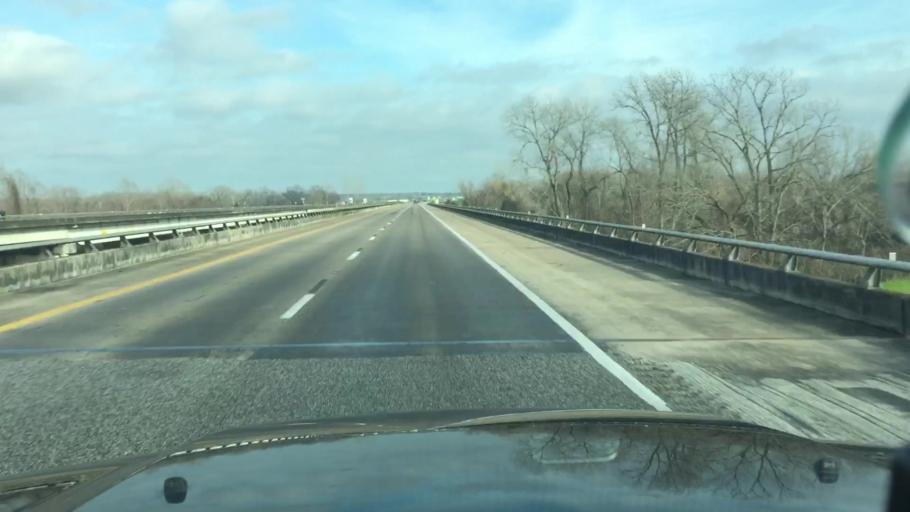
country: US
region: Texas
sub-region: Waller County
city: Hempstead
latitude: 30.1289
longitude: -96.1892
